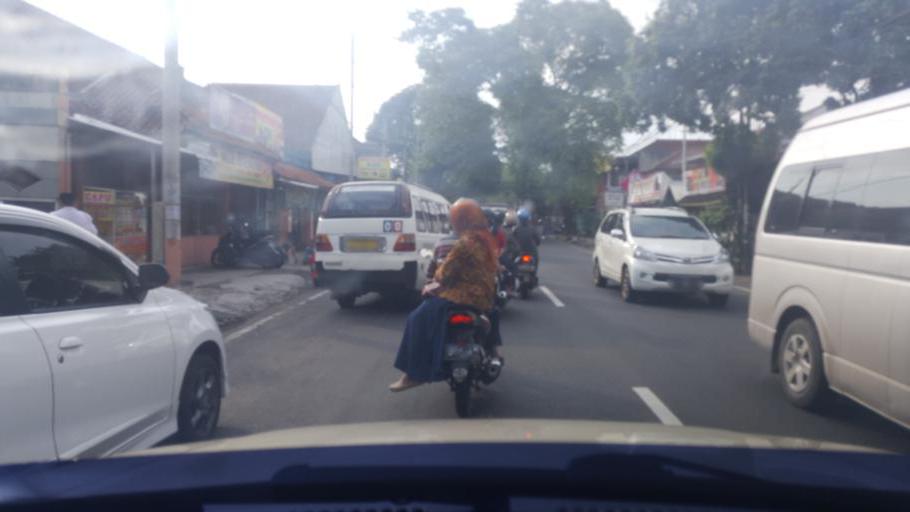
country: ID
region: West Java
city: Mancogeh
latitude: -7.3150
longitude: 108.2148
